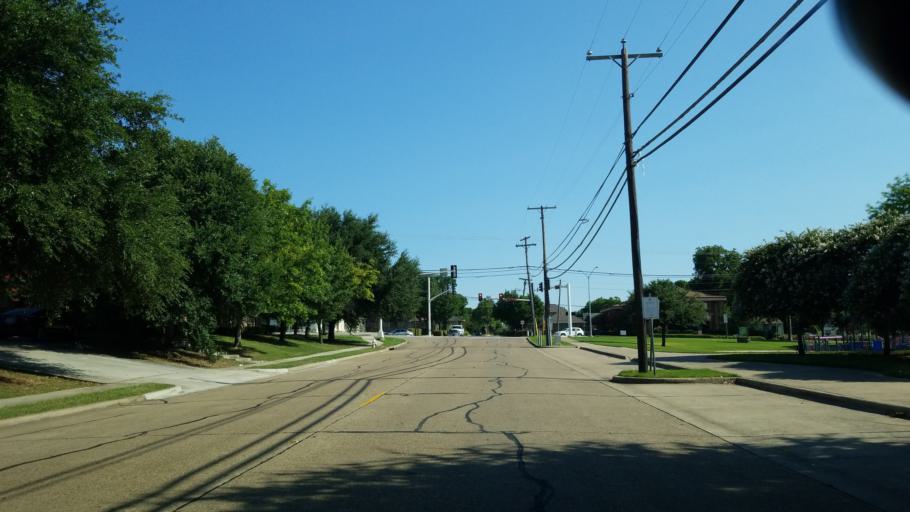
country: US
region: Texas
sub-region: Dallas County
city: Farmers Branch
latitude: 32.9251
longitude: -96.8875
